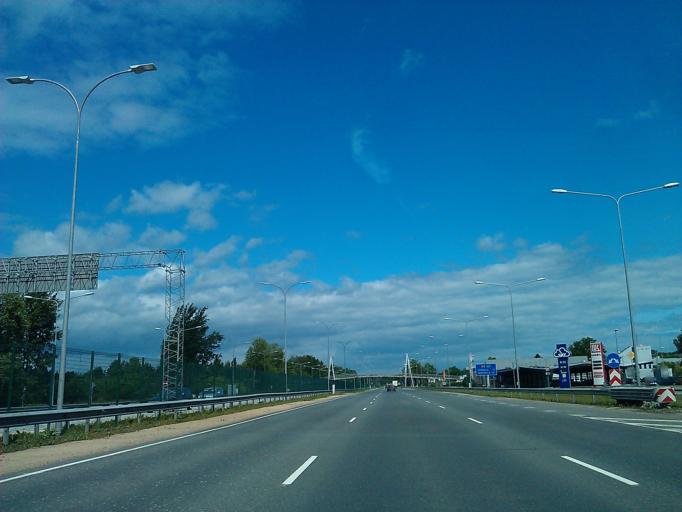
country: LV
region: Marupe
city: Marupe
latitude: 56.9376
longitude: 24.0018
